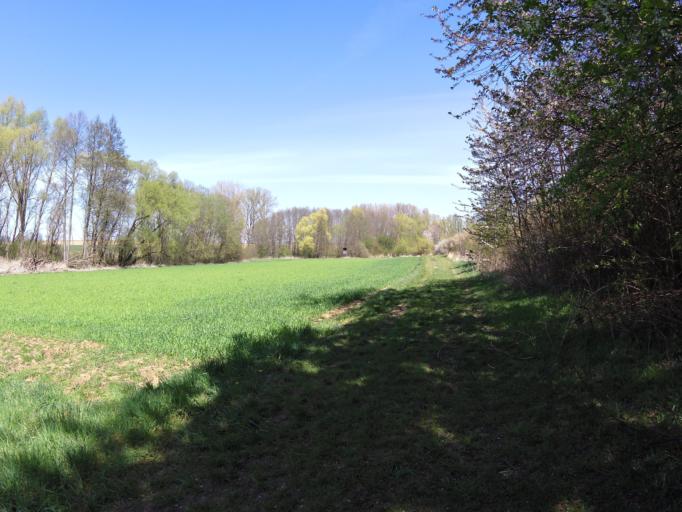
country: DE
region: Bavaria
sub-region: Regierungsbezirk Unterfranken
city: Kurnach
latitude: 49.8609
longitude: 10.0243
